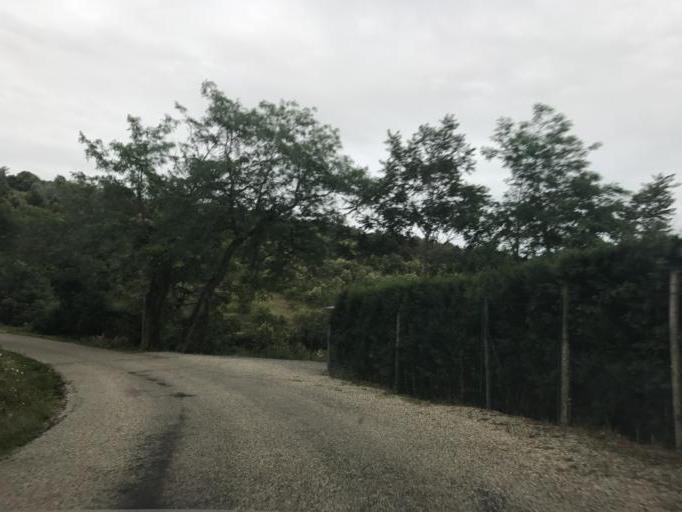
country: FR
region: Rhone-Alpes
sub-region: Departement de l'Ardeche
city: La Voulte-sur-Rhone
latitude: 44.8045
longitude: 4.7503
